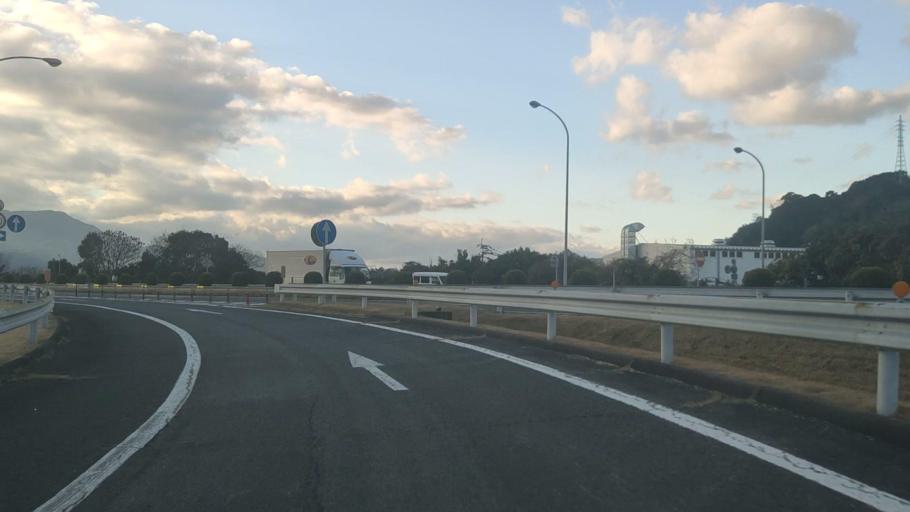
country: JP
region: Saga Prefecture
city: Takeocho-takeo
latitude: 33.2866
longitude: 130.1299
